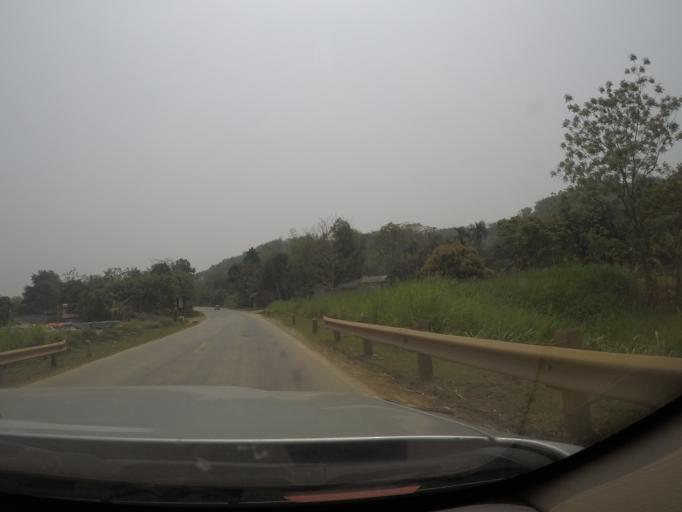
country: VN
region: Thanh Hoa
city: Thi Tran Thuong Xuan
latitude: 19.9600
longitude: 105.3992
